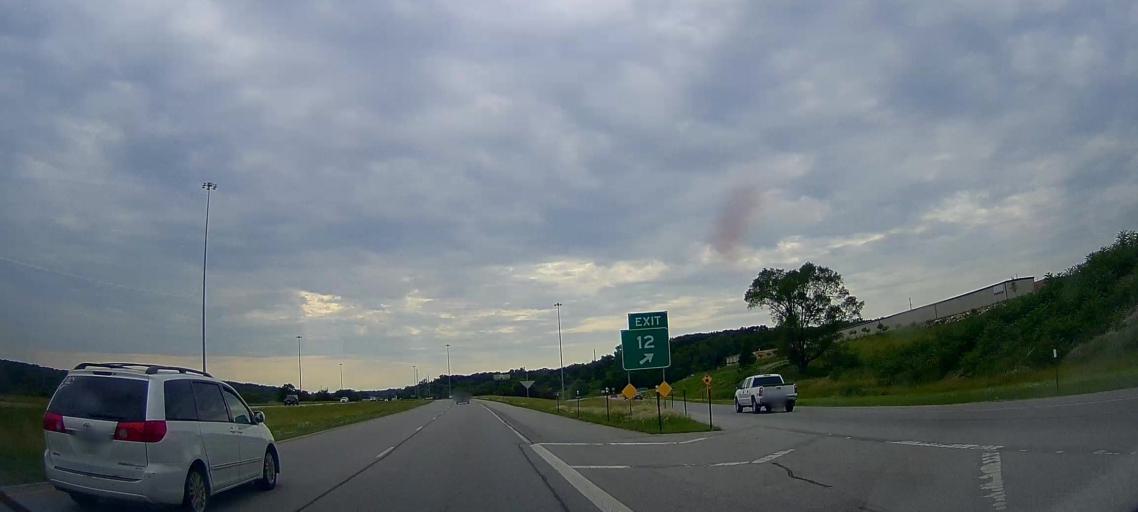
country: US
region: Iowa
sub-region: Pottawattamie County
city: Carter Lake
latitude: 41.3469
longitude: -95.9788
